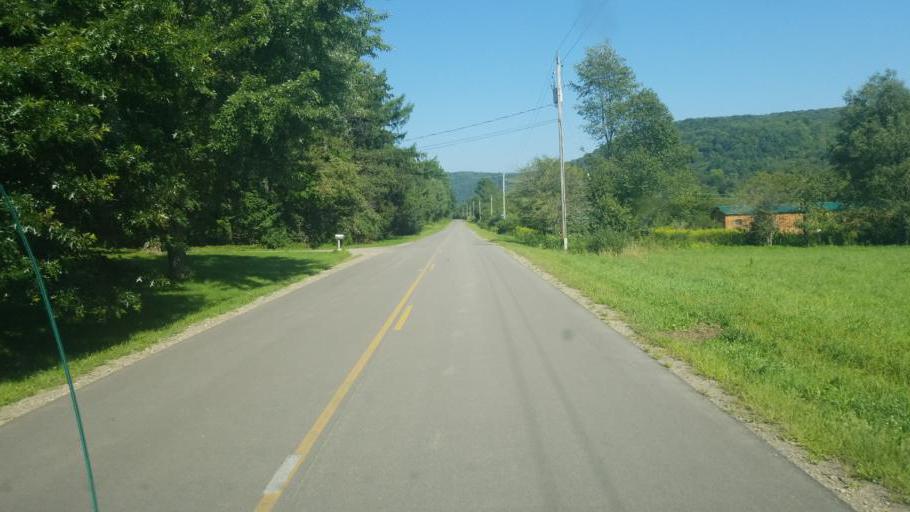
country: US
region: New York
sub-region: Allegany County
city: Wellsville
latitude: 42.0135
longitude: -78.0163
